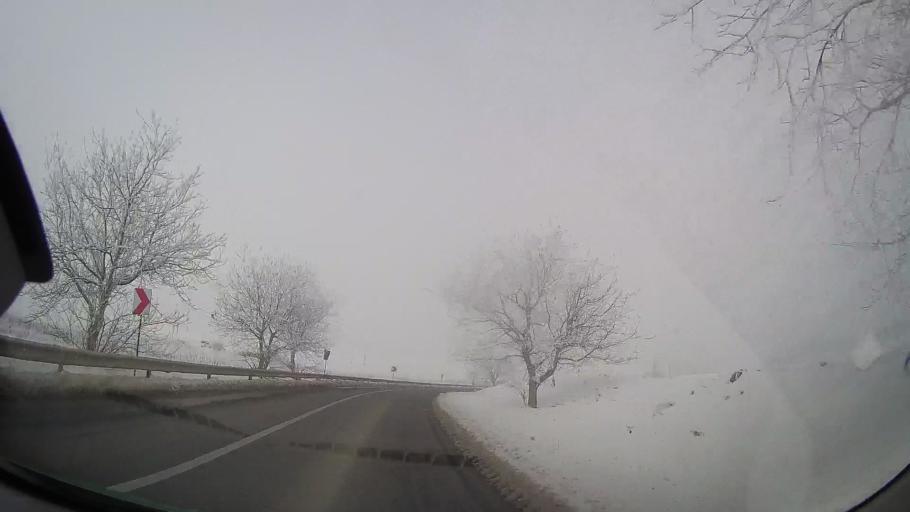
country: RO
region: Iasi
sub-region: Comuna Stolniceni-Prajescu
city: Stolniceni-Prajescu
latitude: 47.1879
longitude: 26.7370
